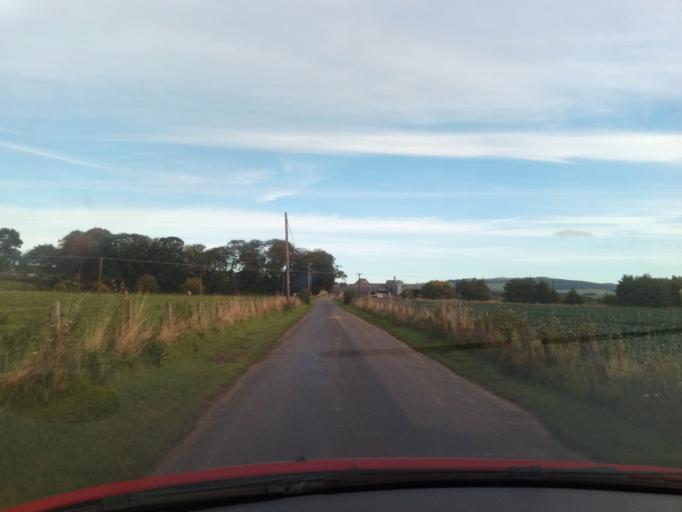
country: GB
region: Scotland
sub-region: The Scottish Borders
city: Kelso
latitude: 55.5228
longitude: -2.4006
